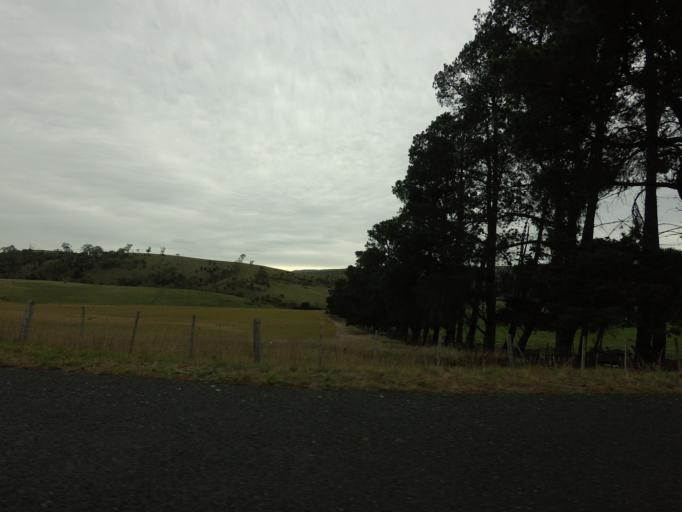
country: AU
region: Tasmania
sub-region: Derwent Valley
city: New Norfolk
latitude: -42.5993
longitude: 147.0699
